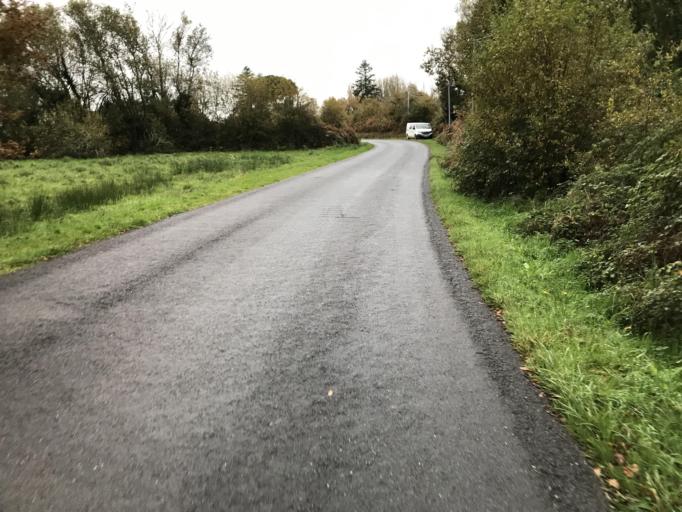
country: FR
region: Brittany
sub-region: Departement du Finistere
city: Logonna-Daoulas
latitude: 48.3308
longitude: -4.2983
